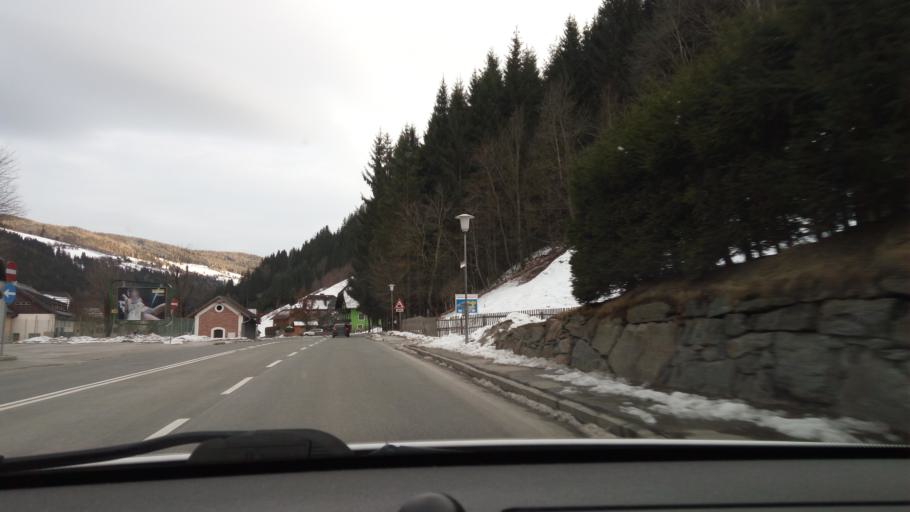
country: AT
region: Salzburg
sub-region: Politischer Bezirk Tamsweg
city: Tamsweg
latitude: 47.1234
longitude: 13.8068
